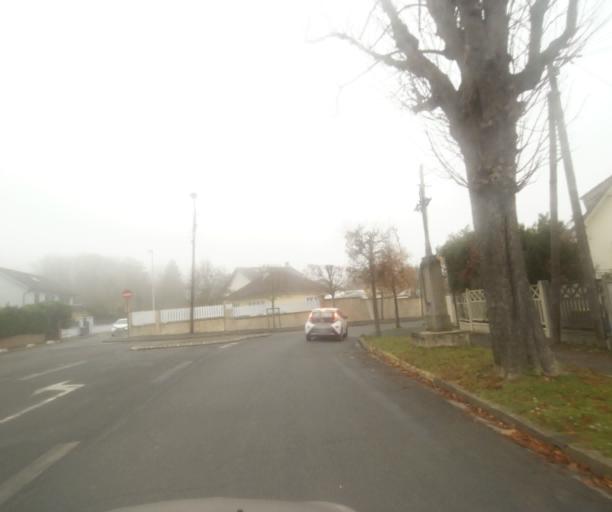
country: FR
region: Ile-de-France
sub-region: Departement de Seine-Saint-Denis
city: Coubron
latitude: 48.9132
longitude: 2.5792
